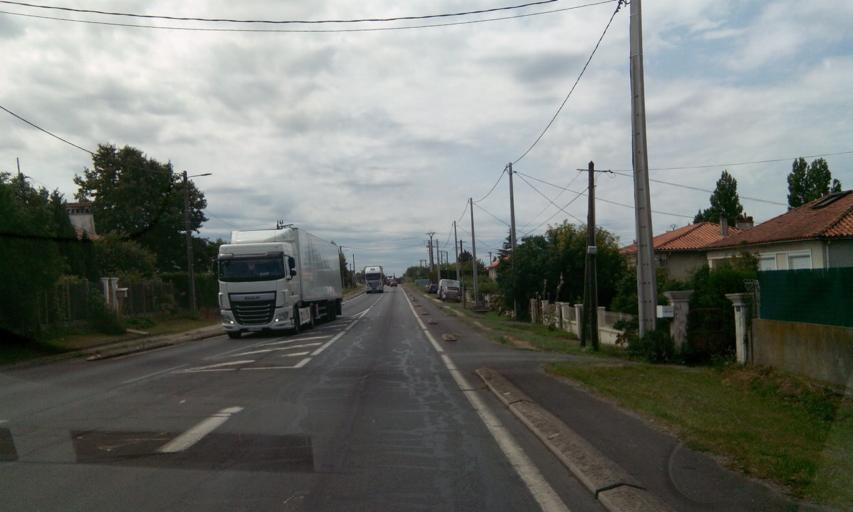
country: FR
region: Poitou-Charentes
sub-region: Departement des Deux-Sevres
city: Melle
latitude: 46.2150
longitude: -0.1421
